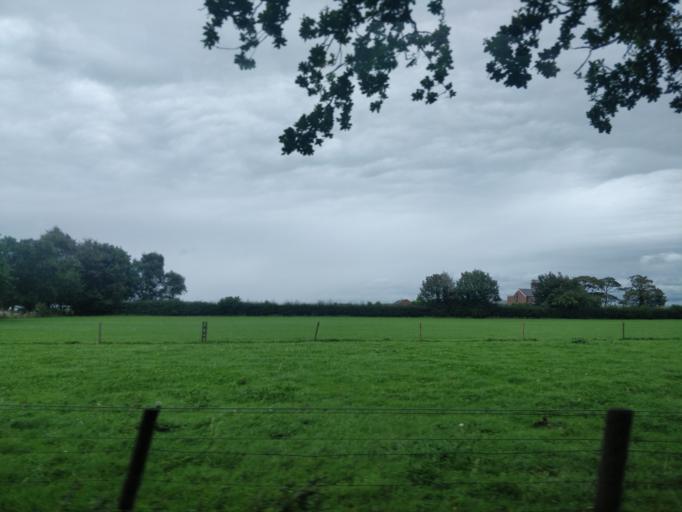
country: GB
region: England
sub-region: Lancashire
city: Ormskirk
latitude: 53.6111
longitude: -2.9168
